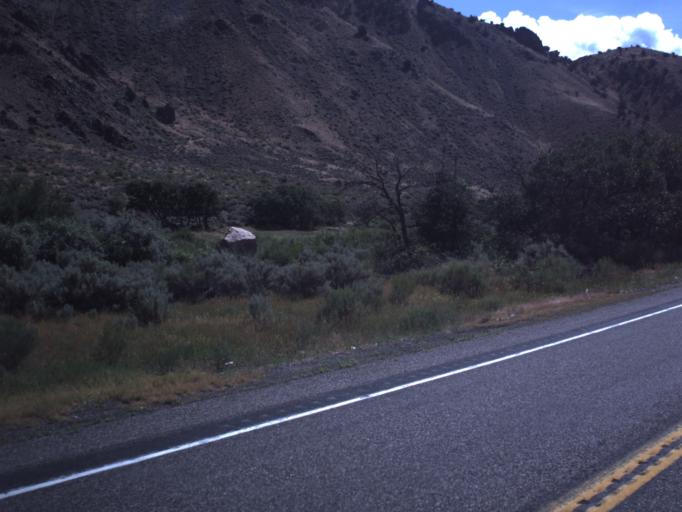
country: US
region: Utah
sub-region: Sevier County
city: Monroe
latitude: 38.4961
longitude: -112.2543
